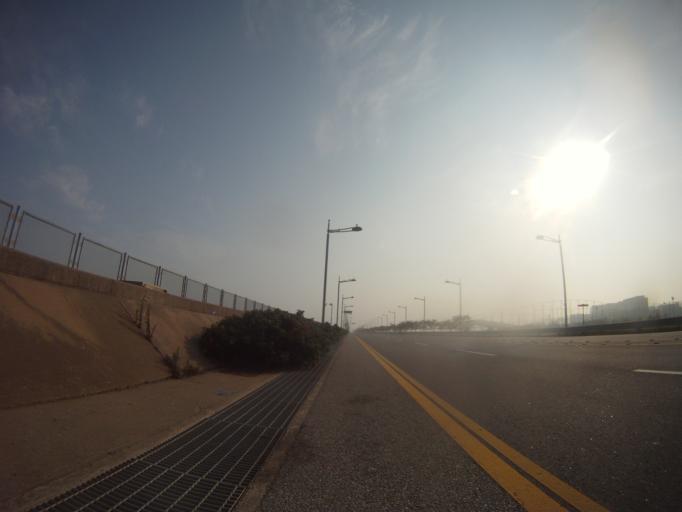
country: KR
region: Incheon
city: Incheon
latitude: 37.4328
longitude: 126.4630
